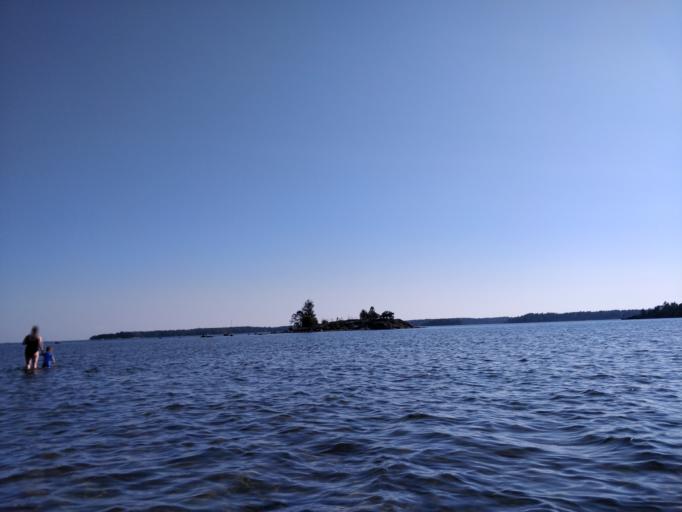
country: FI
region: Uusimaa
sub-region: Helsinki
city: Vantaa
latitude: 60.1844
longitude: 25.1432
